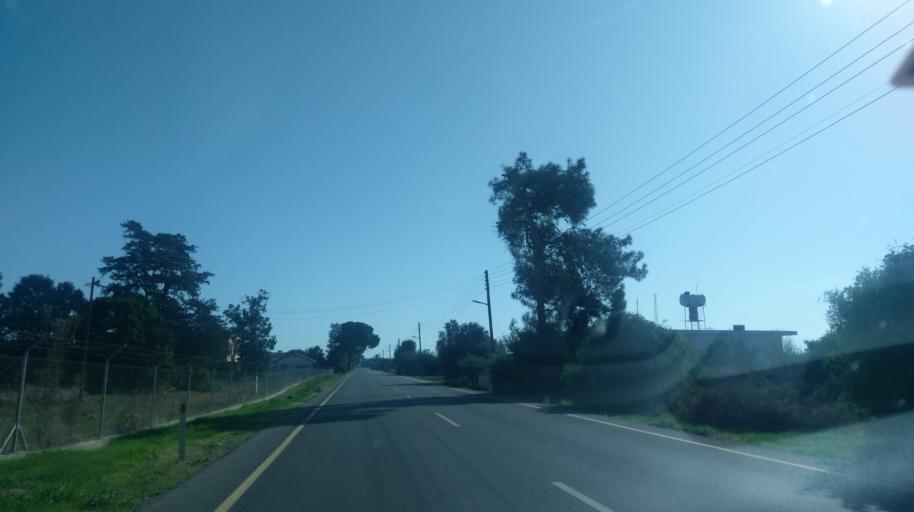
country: CY
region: Ammochostos
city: Famagusta
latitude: 35.0943
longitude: 33.9519
